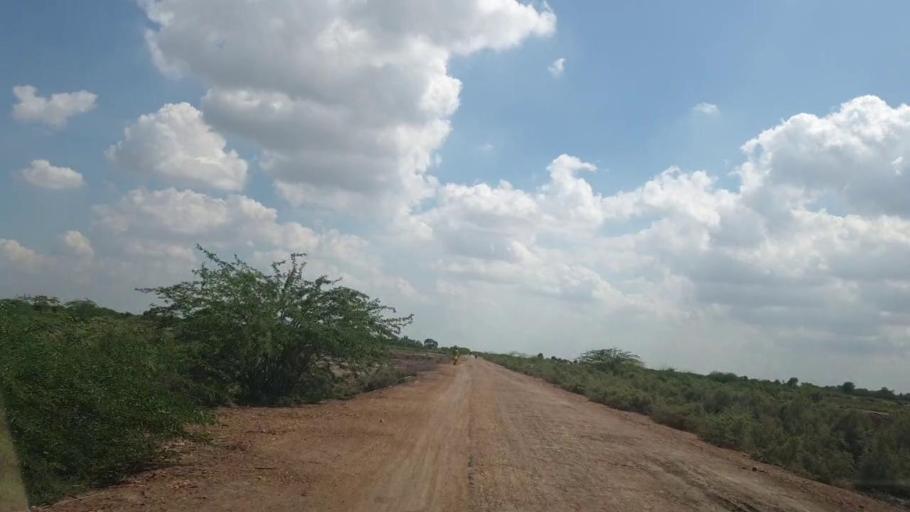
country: PK
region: Sindh
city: Pithoro
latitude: 25.6052
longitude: 69.4073
